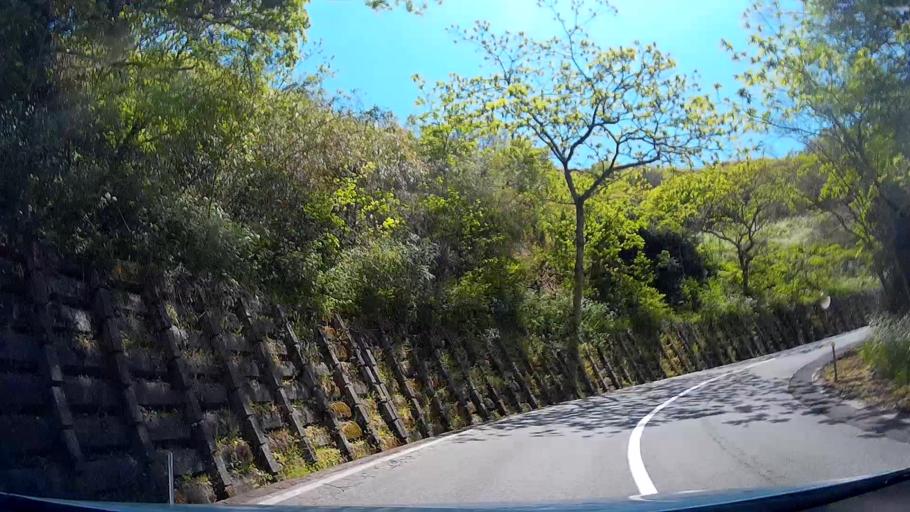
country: JP
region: Ishikawa
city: Nanao
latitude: 37.5245
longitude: 137.2567
